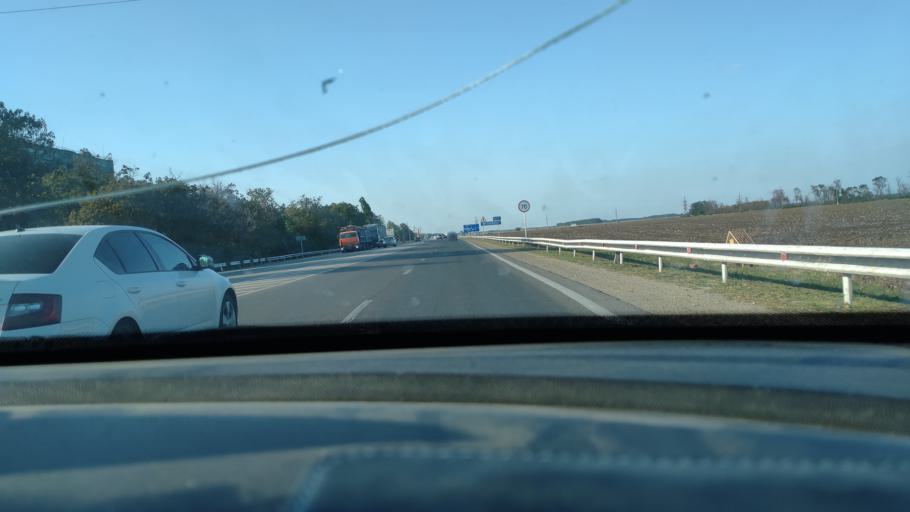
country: RU
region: Krasnodarskiy
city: Timashevsk
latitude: 45.6178
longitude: 38.9867
